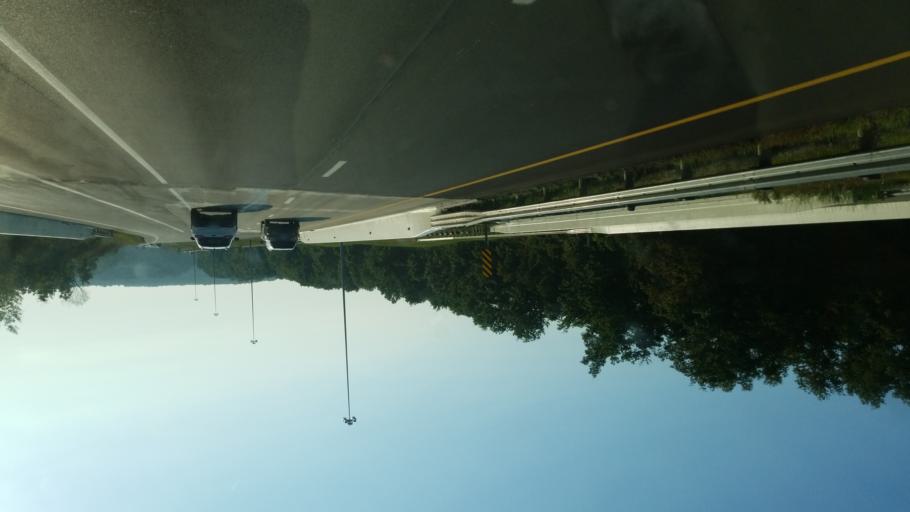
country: US
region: Ohio
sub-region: Summit County
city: Richfield
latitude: 41.2295
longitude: -81.6247
